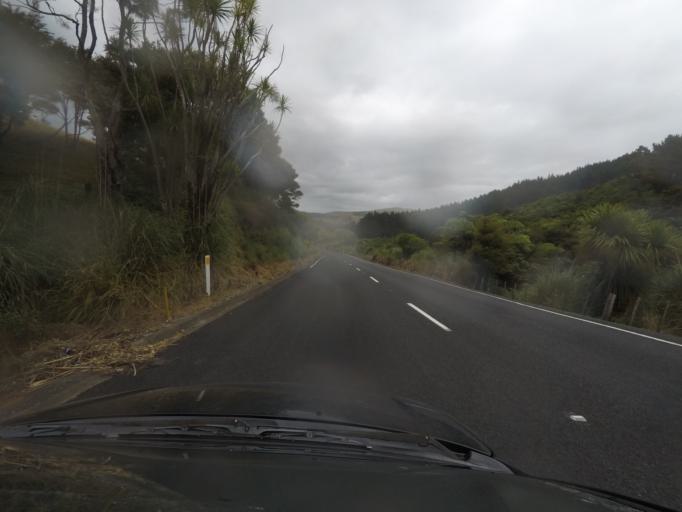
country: NZ
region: Auckland
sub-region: Auckland
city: Warkworth
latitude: -36.2776
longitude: 174.6891
